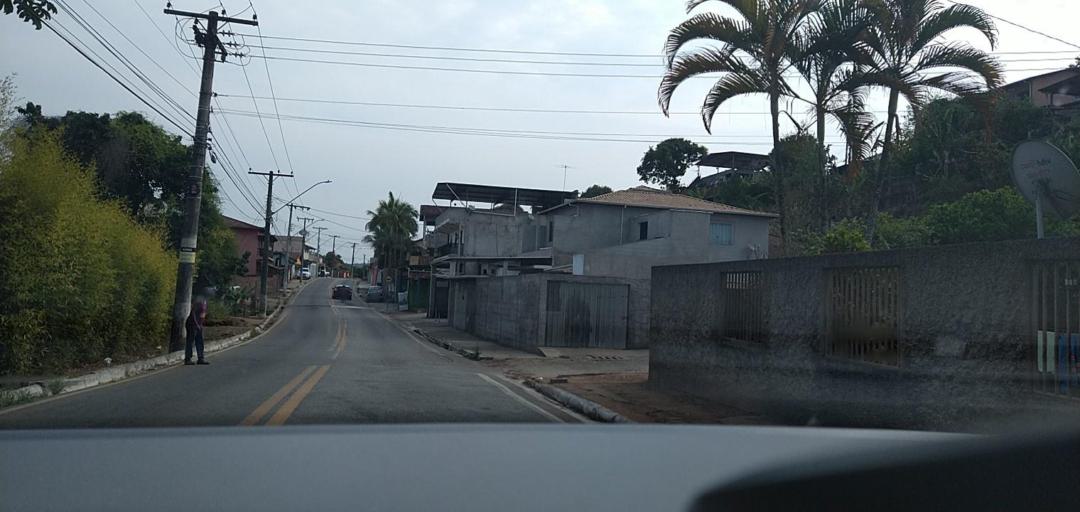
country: BR
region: Minas Gerais
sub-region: Rio Piracicaba
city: Rio Piracicaba
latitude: -19.8999
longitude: -43.1460
